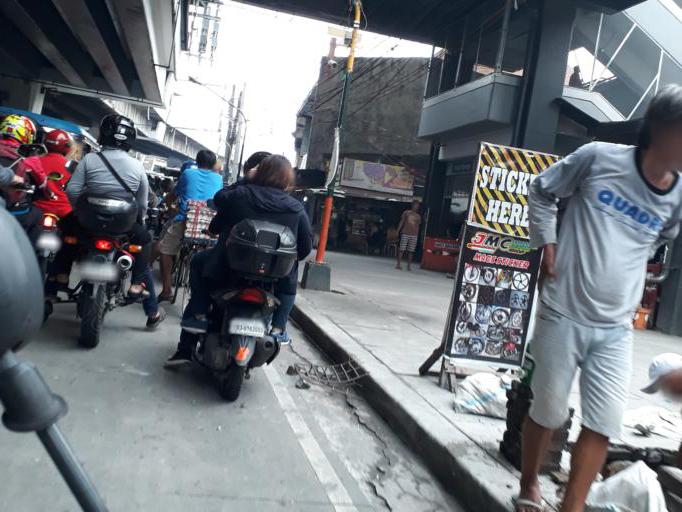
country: PH
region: Metro Manila
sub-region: City of Manila
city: Manila
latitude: 14.6305
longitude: 120.9815
